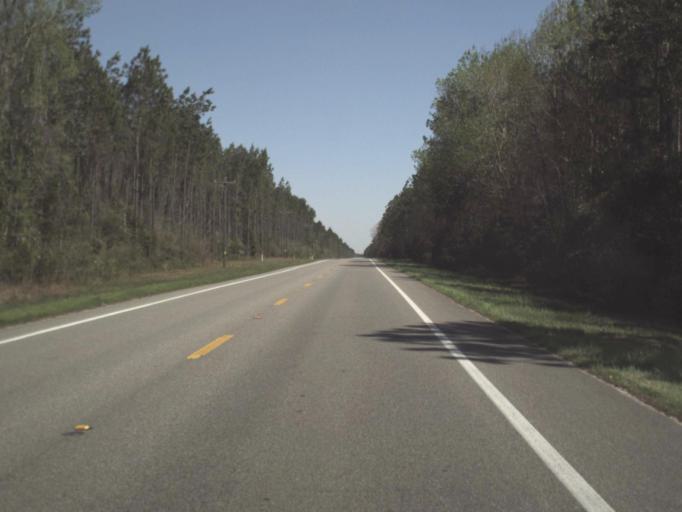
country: US
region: Florida
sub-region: Liberty County
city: Bristol
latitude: 30.3870
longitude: -84.7722
